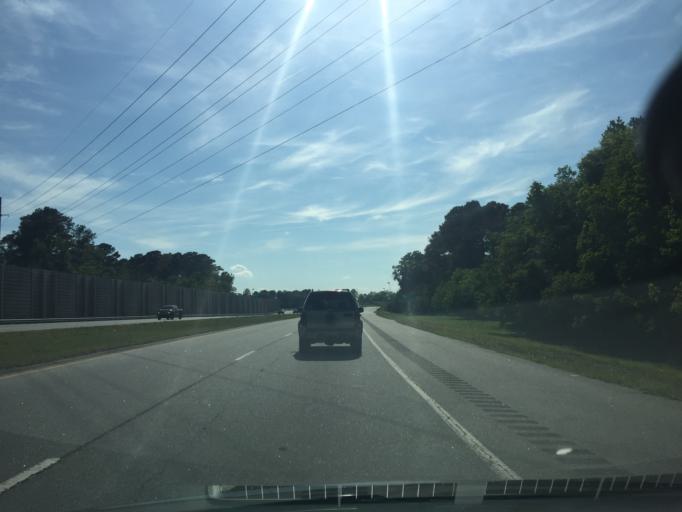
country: US
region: Georgia
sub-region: Chatham County
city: Isle of Hope
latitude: 31.9749
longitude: -81.0986
